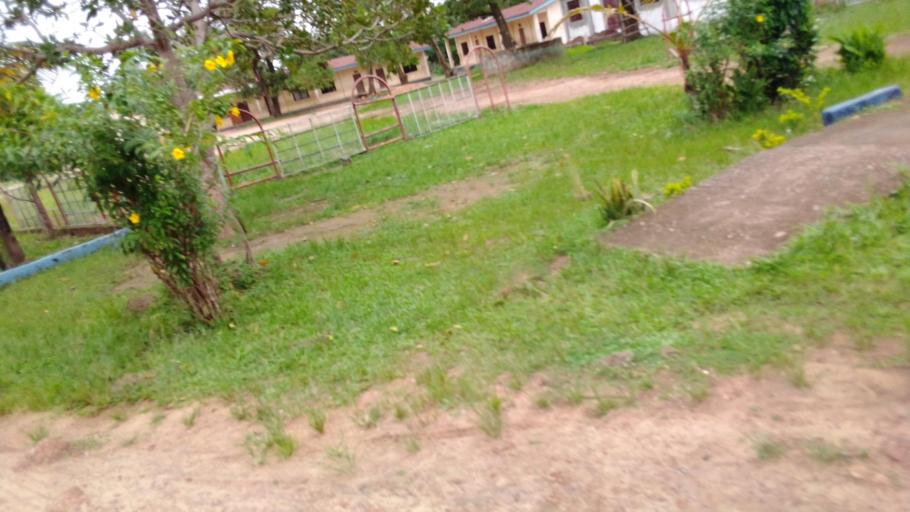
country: SL
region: Eastern Province
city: Kenema
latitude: 7.8623
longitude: -11.2023
